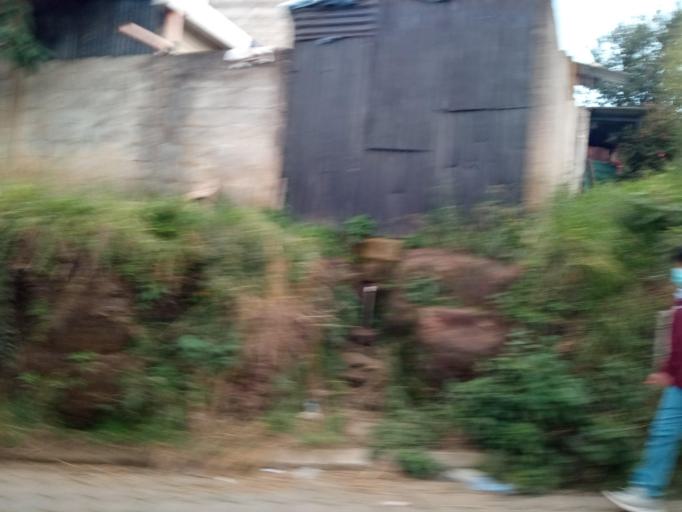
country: GT
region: Quetzaltenango
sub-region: Municipio de La Esperanza
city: La Esperanza
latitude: 14.8558
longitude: -91.5470
